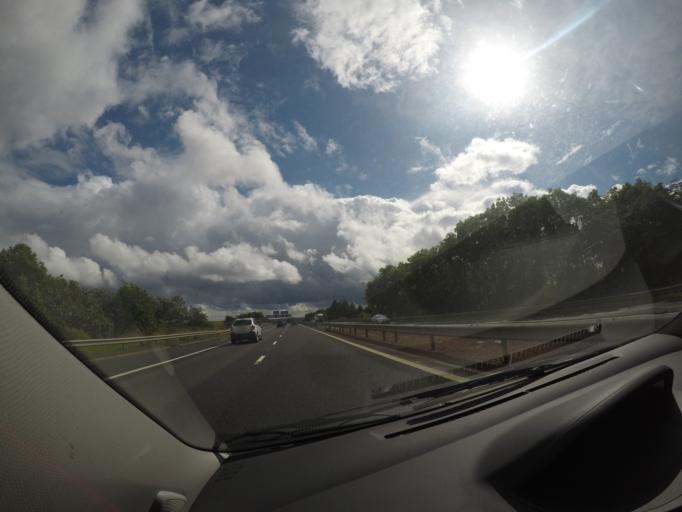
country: GB
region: Scotland
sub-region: South Lanarkshire
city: Uddingston
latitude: 55.8595
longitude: -4.0854
